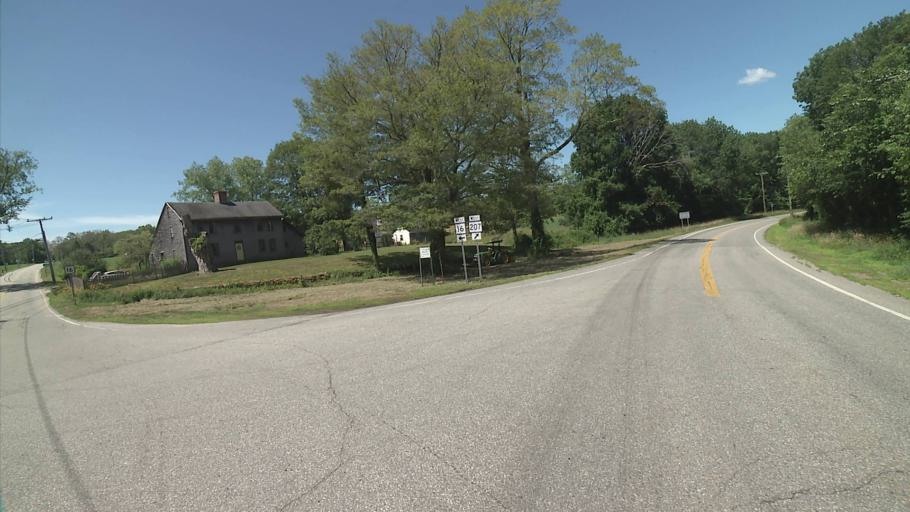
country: US
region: Connecticut
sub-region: New London County
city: Colchester
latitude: 41.6174
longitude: -72.2716
